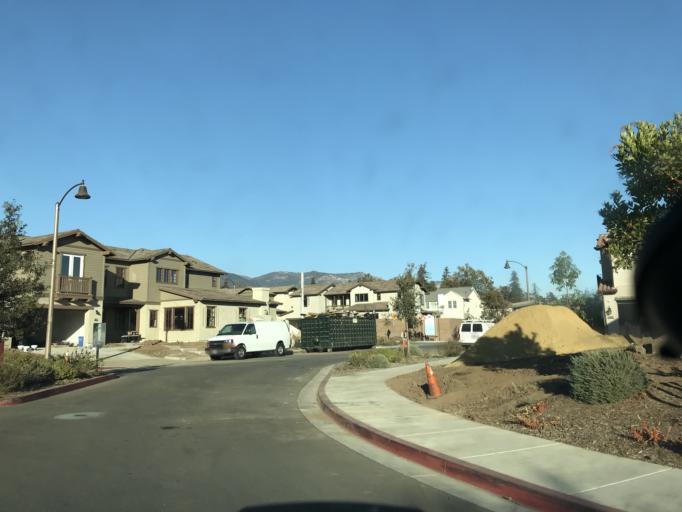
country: US
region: California
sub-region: Santa Barbara County
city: Goleta
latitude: 34.4488
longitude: -119.8144
